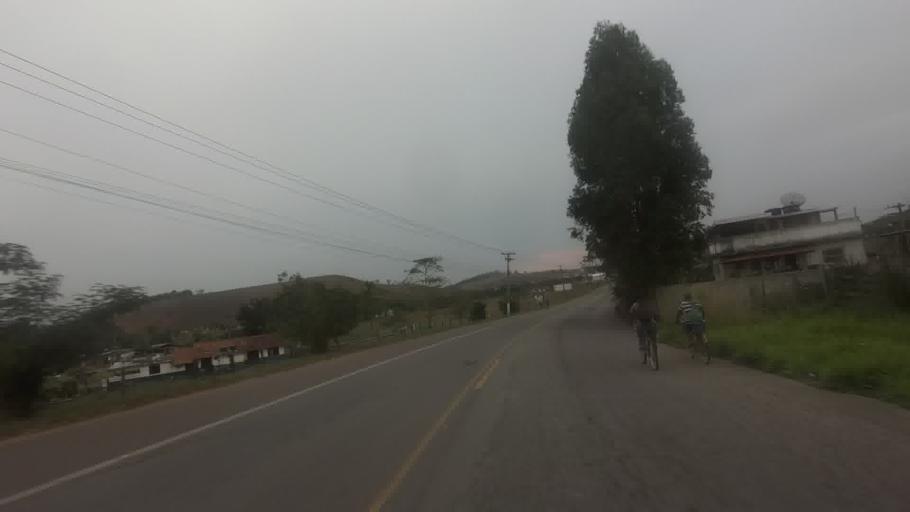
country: BR
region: Rio de Janeiro
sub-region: Santo Antonio De Padua
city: Santo Antonio de Padua
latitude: -21.6584
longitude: -42.3308
